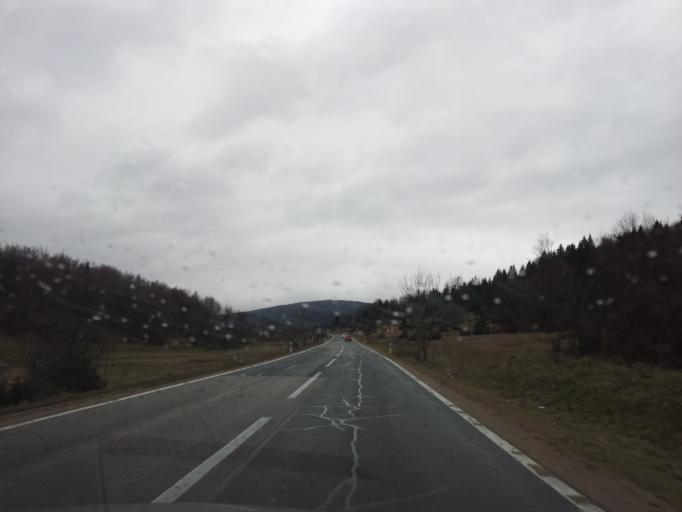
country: HR
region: Licko-Senjska
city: Jezerce
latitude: 44.8027
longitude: 15.6832
